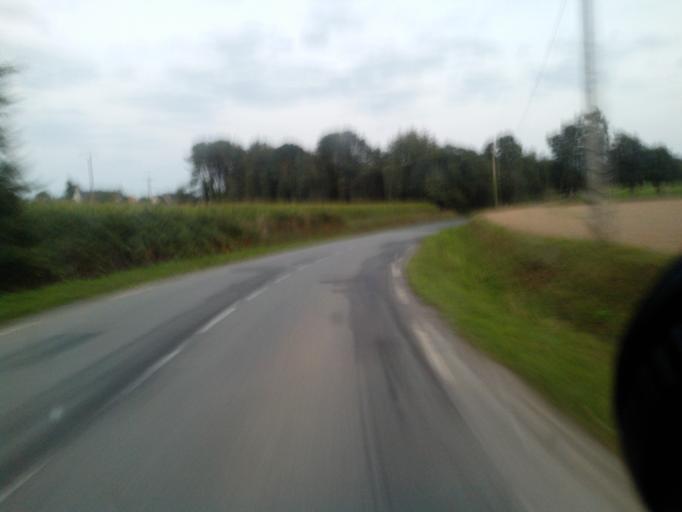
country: FR
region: Brittany
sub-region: Departement d'Ille-et-Vilaine
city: Iffendic
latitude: 48.1195
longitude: -2.0361
